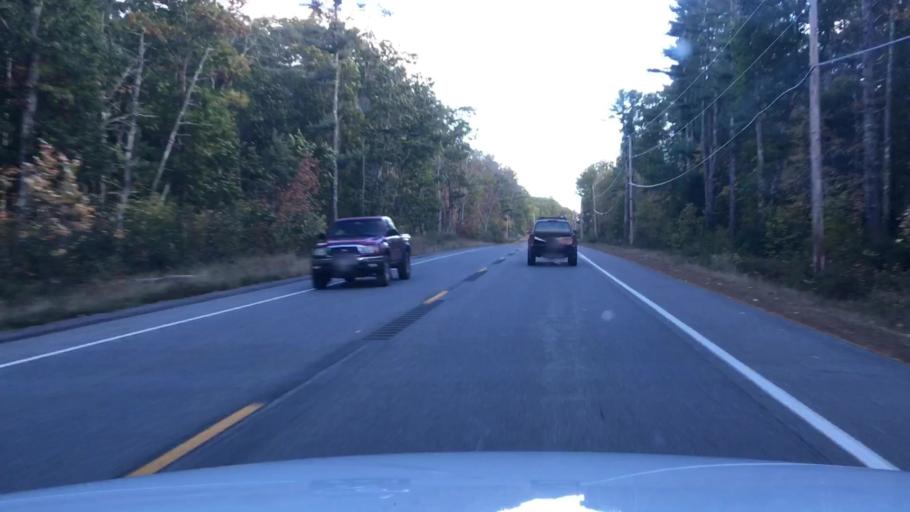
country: US
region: Maine
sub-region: York County
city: Wells Beach Station
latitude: 43.3420
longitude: -70.6398
